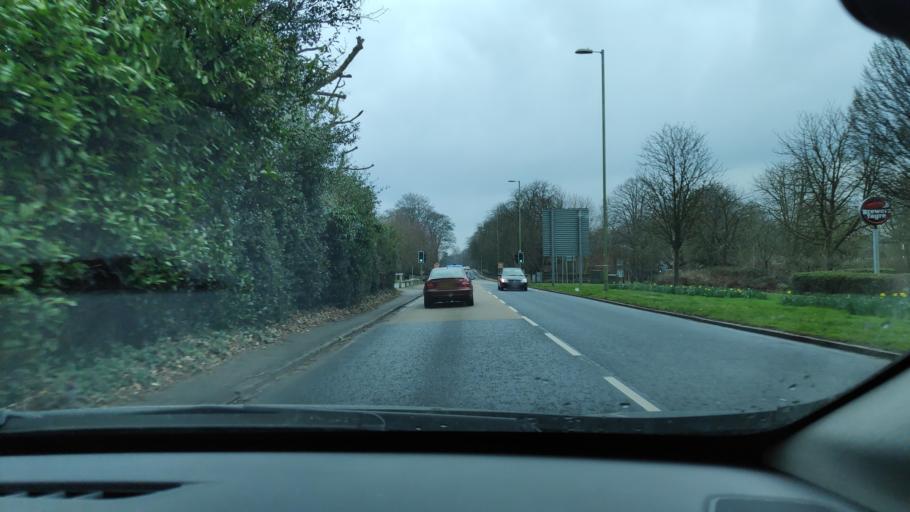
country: GB
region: England
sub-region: Hampshire
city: Aldershot
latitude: 51.2514
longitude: -0.7773
